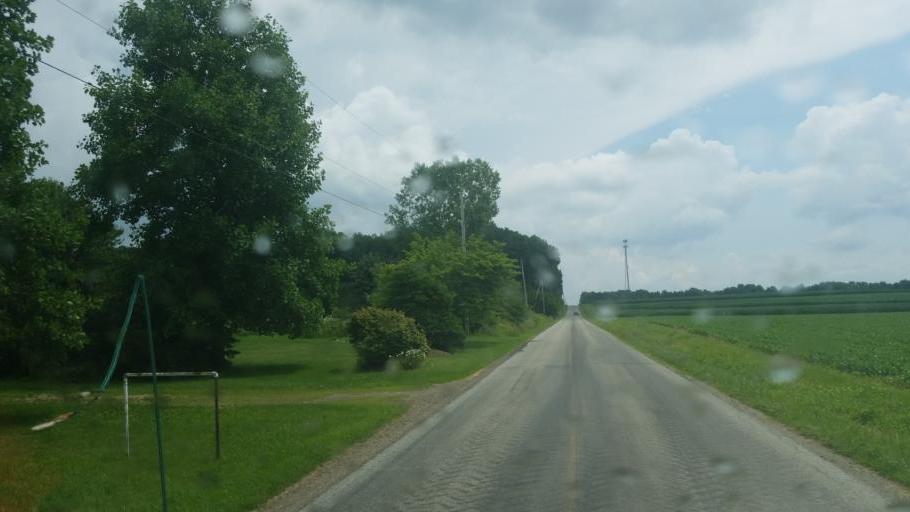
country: US
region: Ohio
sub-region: Wayne County
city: West Salem
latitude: 40.8581
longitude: -82.1253
